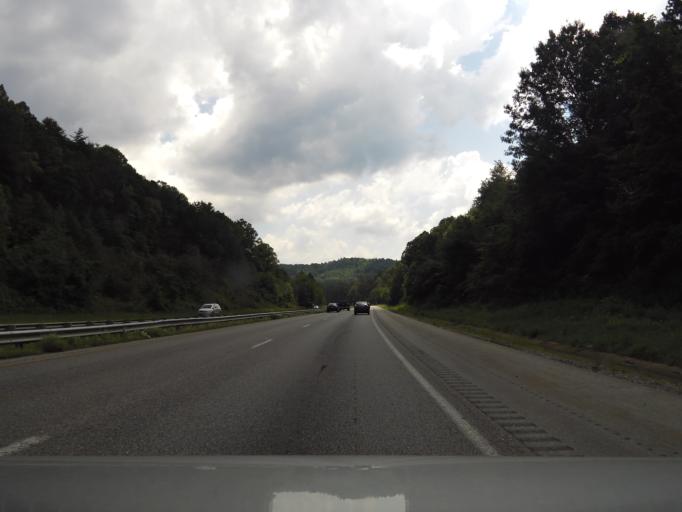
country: US
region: North Carolina
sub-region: Henderson County
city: East Flat Rock
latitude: 35.2610
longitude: -82.3563
